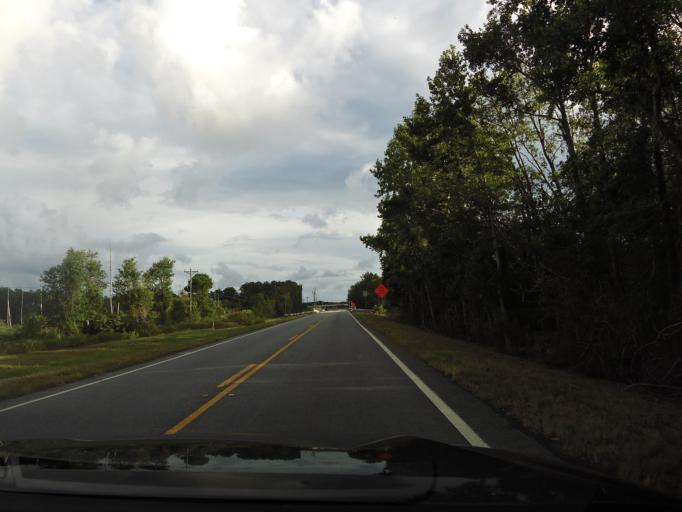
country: US
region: Georgia
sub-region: Liberty County
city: Midway
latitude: 31.6599
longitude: -81.3973
